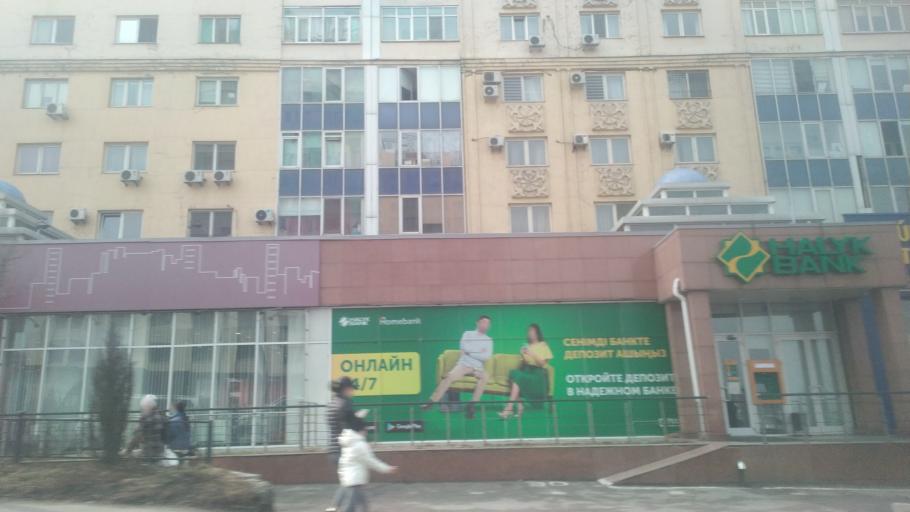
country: KZ
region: Almaty Qalasy
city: Almaty
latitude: 43.1976
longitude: 76.8942
